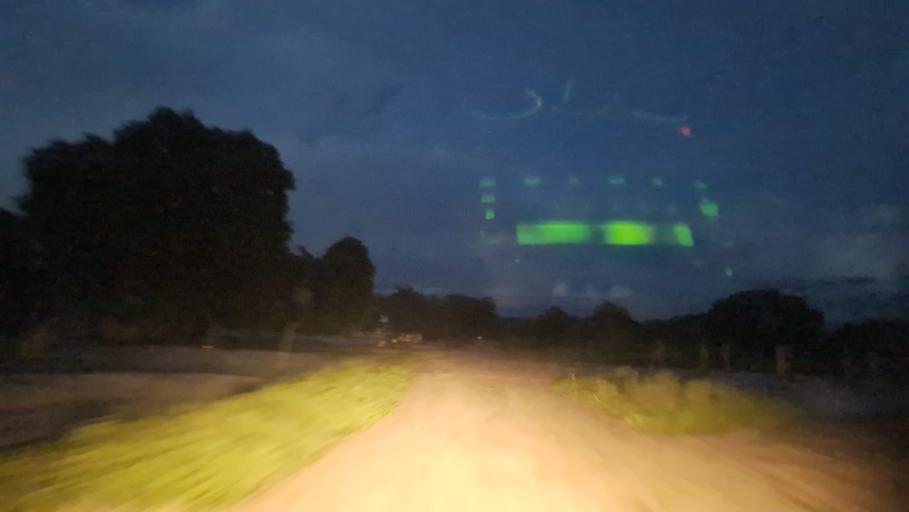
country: MZ
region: Nampula
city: Nampula
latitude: -14.6645
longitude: 39.8371
